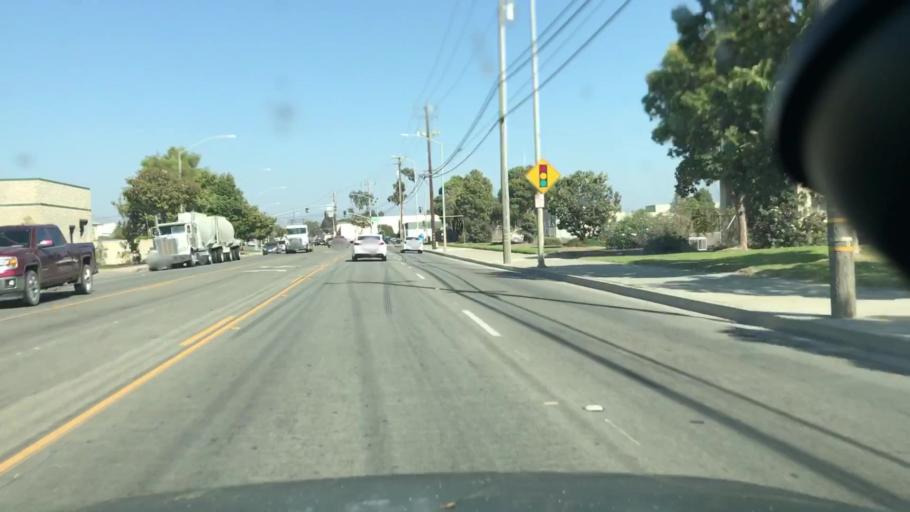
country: US
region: California
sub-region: Santa Barbara County
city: Santa Maria
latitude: 34.9204
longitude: -120.4424
